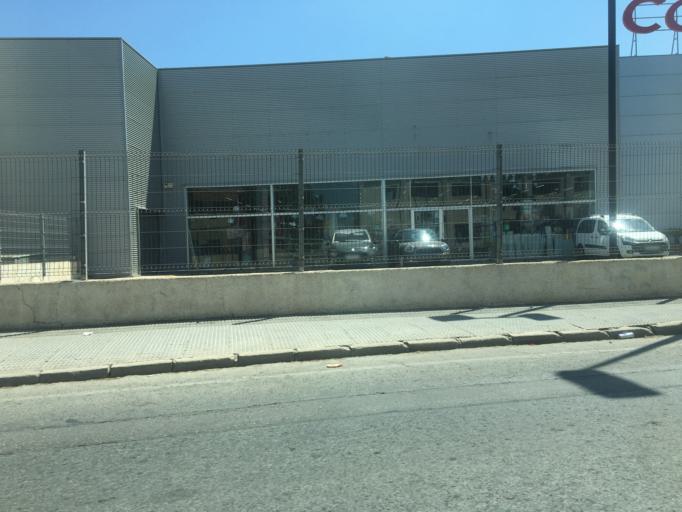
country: ES
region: Murcia
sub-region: Murcia
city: Murcia
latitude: 37.9904
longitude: -1.1097
